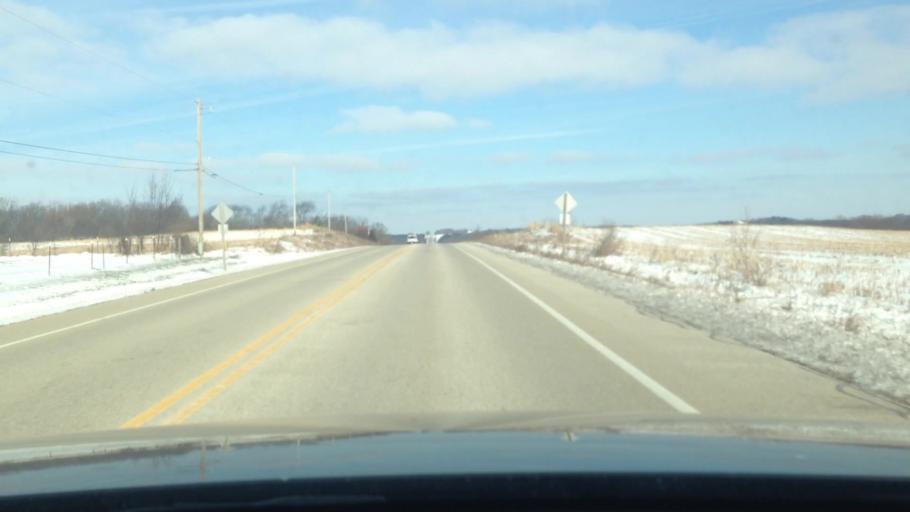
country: US
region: Wisconsin
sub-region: Walworth County
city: East Troy
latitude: 42.7142
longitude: -88.4053
